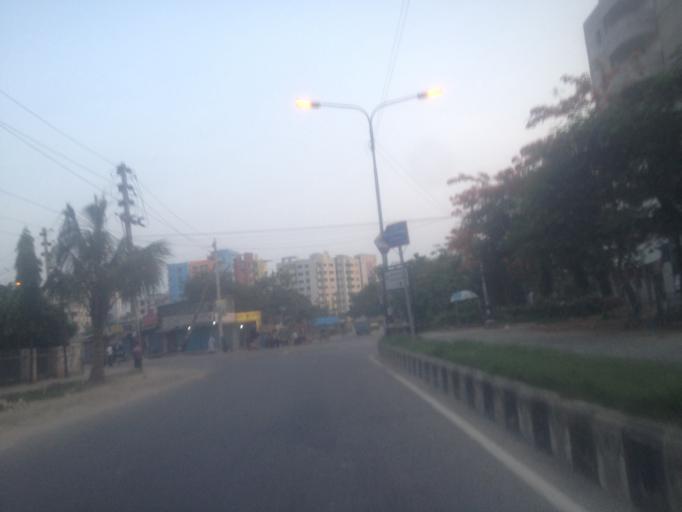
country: BD
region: Dhaka
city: Azimpur
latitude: 23.7768
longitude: 90.3713
